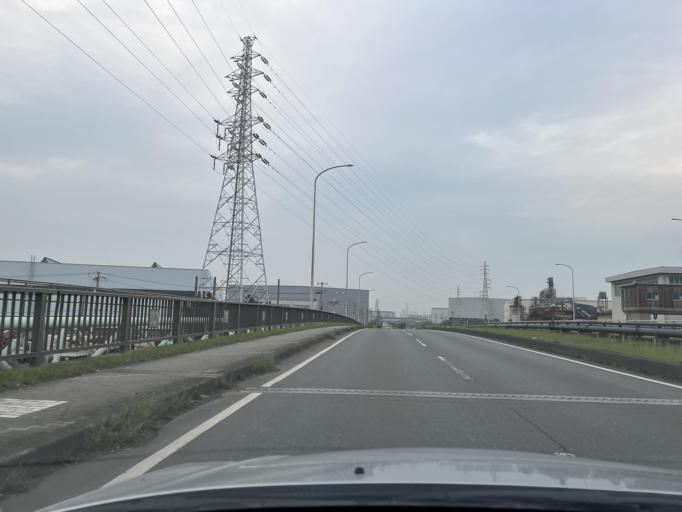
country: JP
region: Chiba
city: Funabashi
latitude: 35.6808
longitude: 139.9628
